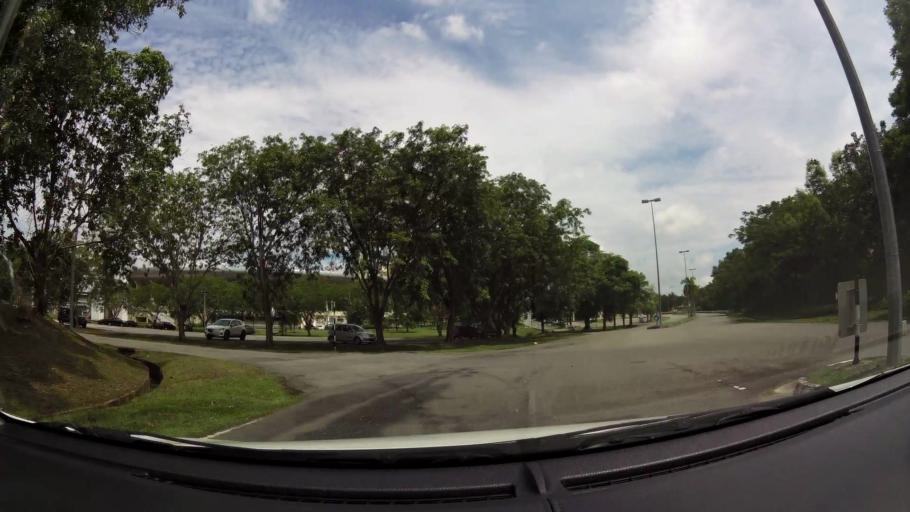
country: BN
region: Brunei and Muara
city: Bandar Seri Begawan
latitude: 4.9312
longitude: 114.9445
